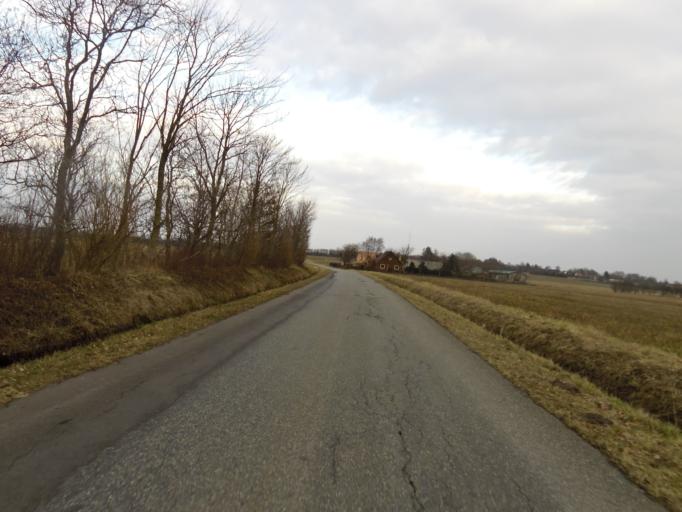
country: DK
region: South Denmark
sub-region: Tonder Kommune
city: Toftlund
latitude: 55.1813
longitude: 9.0515
